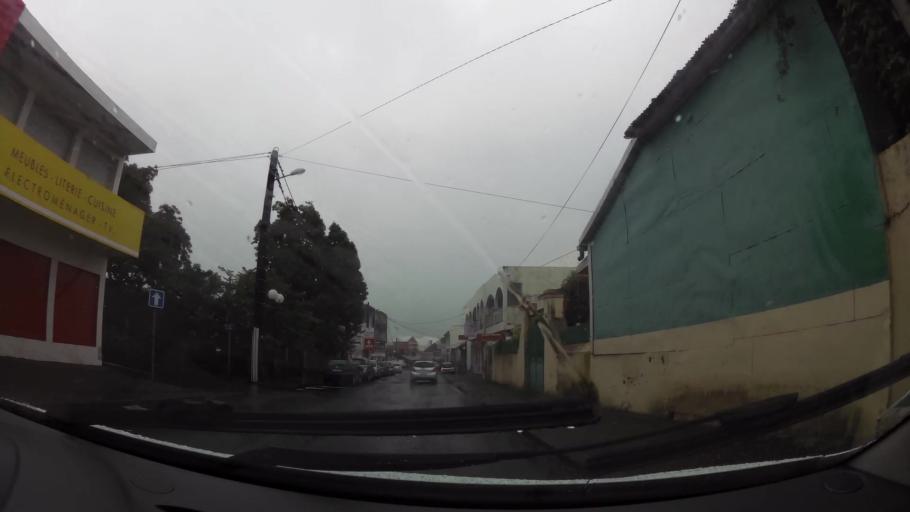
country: RE
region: Reunion
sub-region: Reunion
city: Saint-Andre
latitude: -20.9630
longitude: 55.6494
